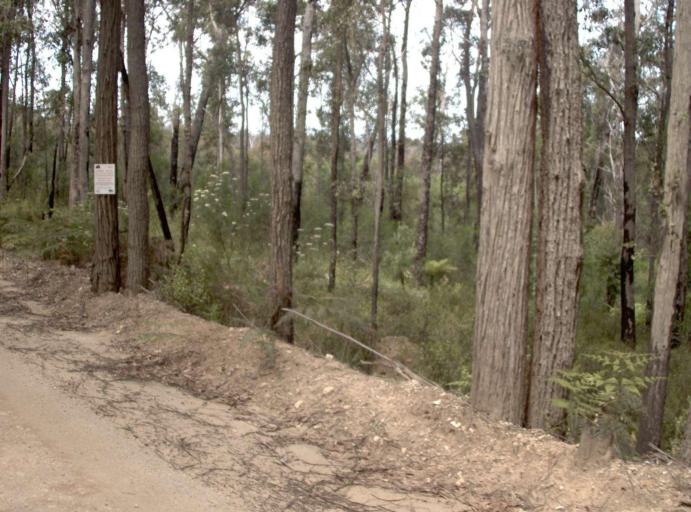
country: AU
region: Victoria
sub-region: East Gippsland
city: Lakes Entrance
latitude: -37.6870
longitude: 148.6197
